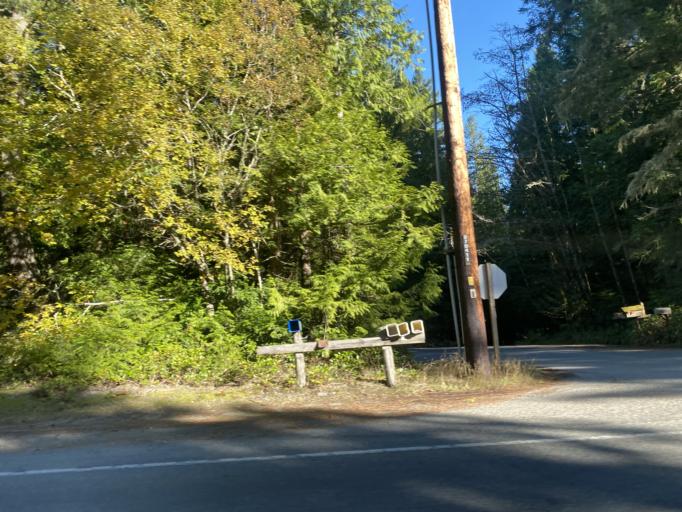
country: US
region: Washington
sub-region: Island County
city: Langley
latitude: 48.0058
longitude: -122.4250
